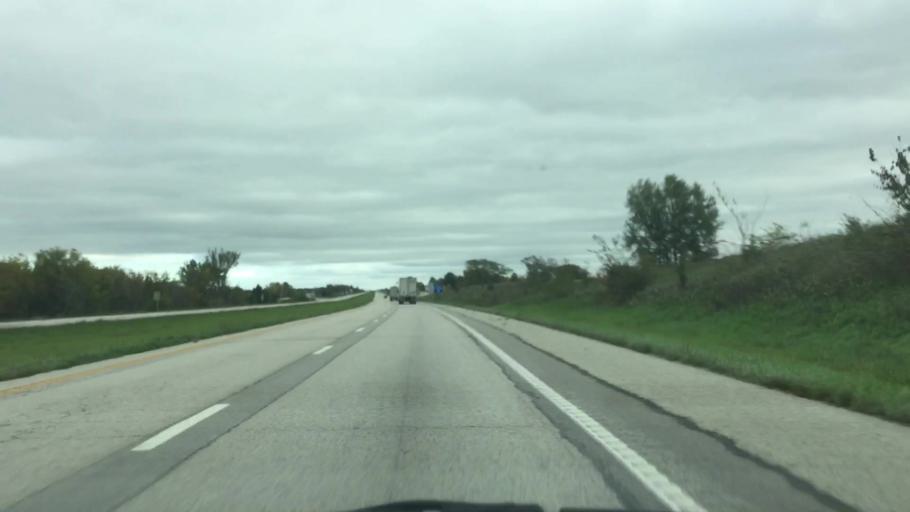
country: US
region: Missouri
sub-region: Harrison County
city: Bethany
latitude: 40.1107
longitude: -94.0657
